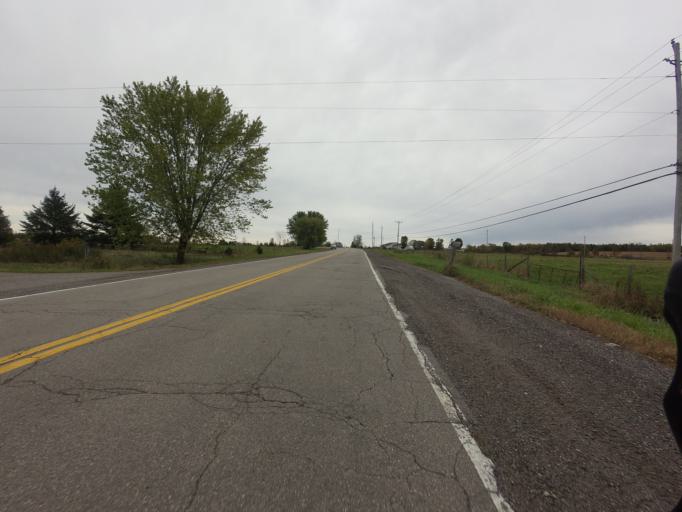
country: CA
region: Ontario
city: Brockville
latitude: 44.6517
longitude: -75.8975
